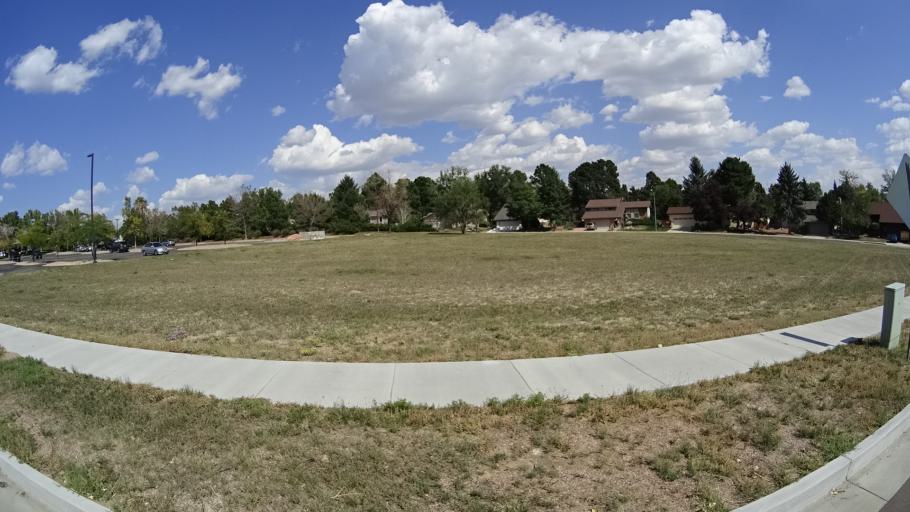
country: US
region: Colorado
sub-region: El Paso County
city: Cimarron Hills
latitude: 38.8764
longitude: -104.7542
